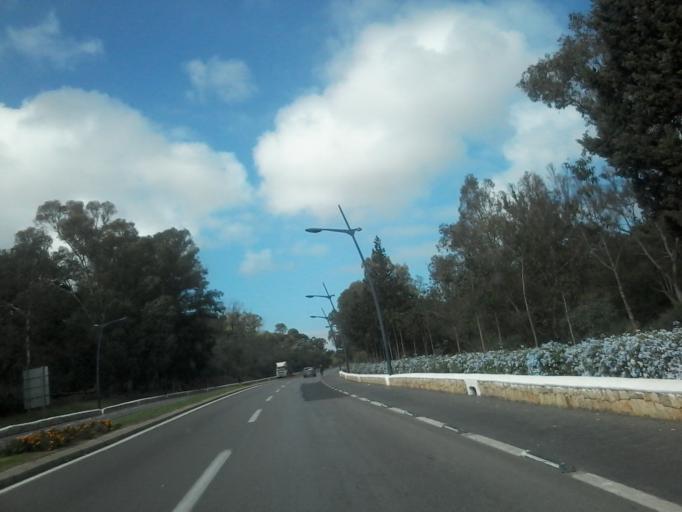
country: MA
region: Tanger-Tetouan
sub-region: Tetouan
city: Martil
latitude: 35.6696
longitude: -5.3202
